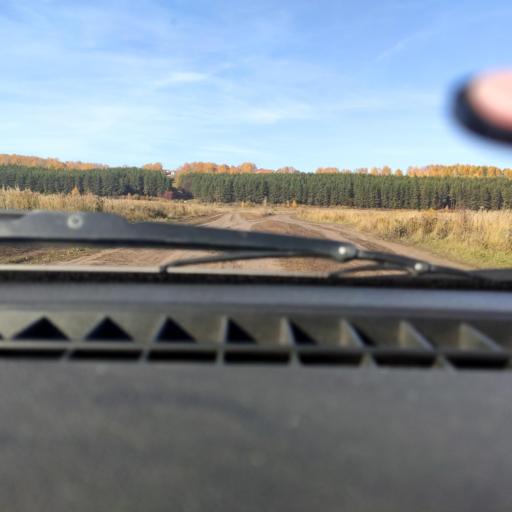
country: RU
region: Bashkortostan
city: Ufa
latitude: 54.8390
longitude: 56.1680
